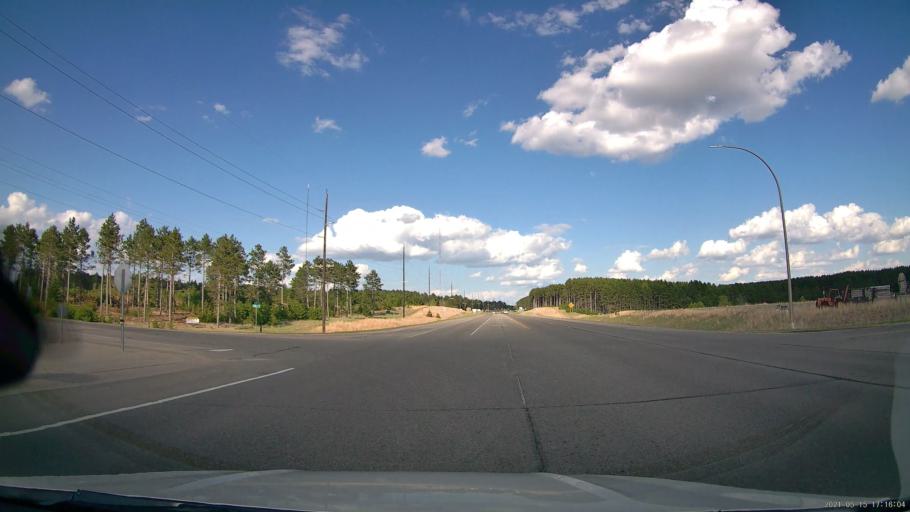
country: US
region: Minnesota
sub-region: Hubbard County
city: Park Rapids
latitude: 46.9254
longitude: -95.0156
